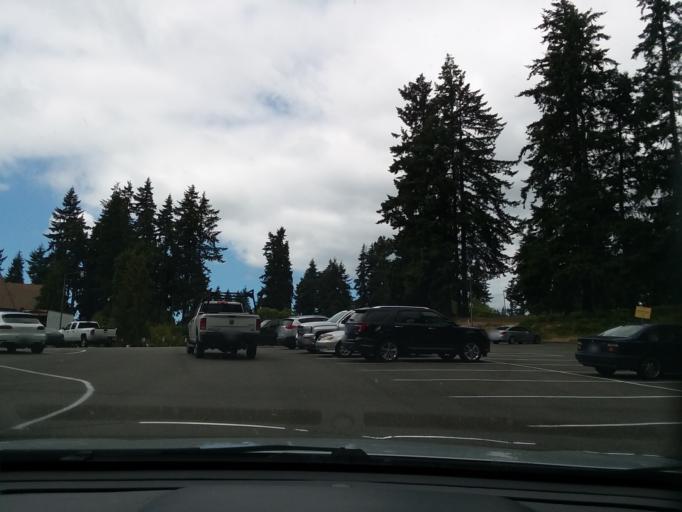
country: US
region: Washington
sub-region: Snohomish County
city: Mountlake Terrace
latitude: 47.7827
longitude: -122.3207
